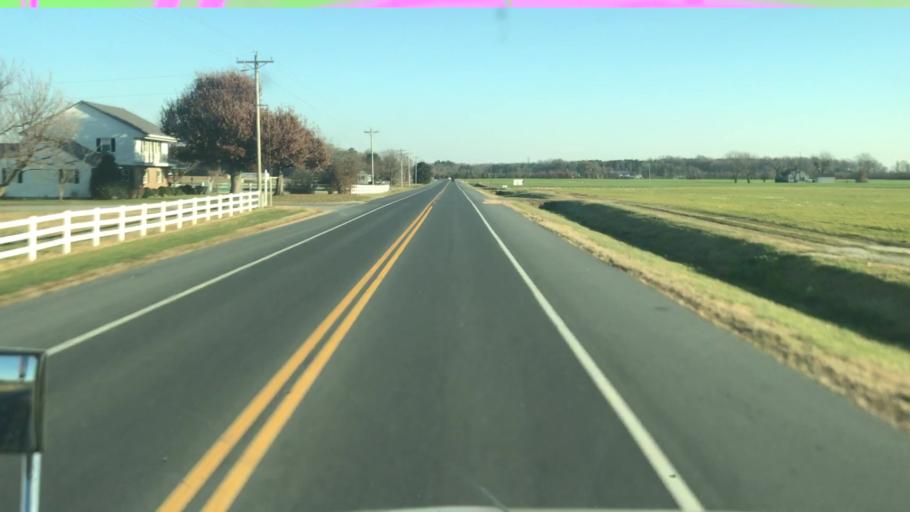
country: US
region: Delaware
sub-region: Sussex County
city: Bridgeville
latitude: 38.7882
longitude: -75.6845
